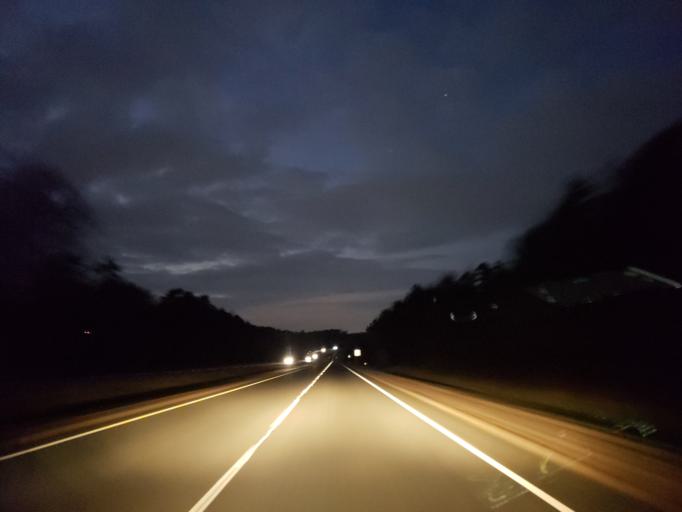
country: US
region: Georgia
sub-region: Polk County
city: Rockmart
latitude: 33.9862
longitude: -85.0185
